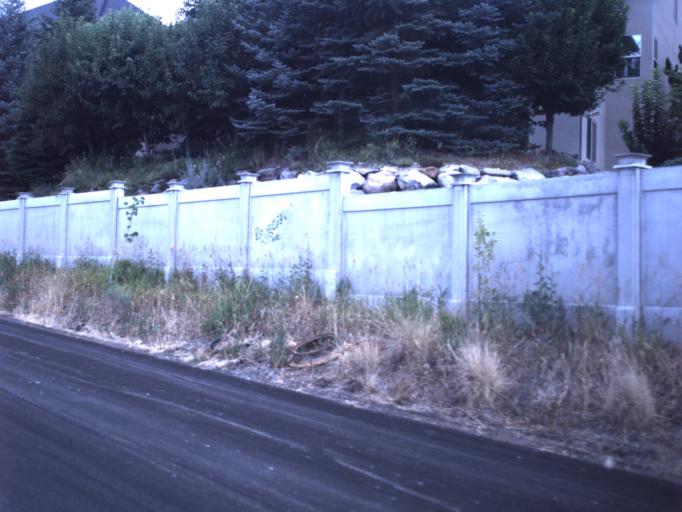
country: US
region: Utah
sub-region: Salt Lake County
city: Granite
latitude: 40.5729
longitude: -111.7898
